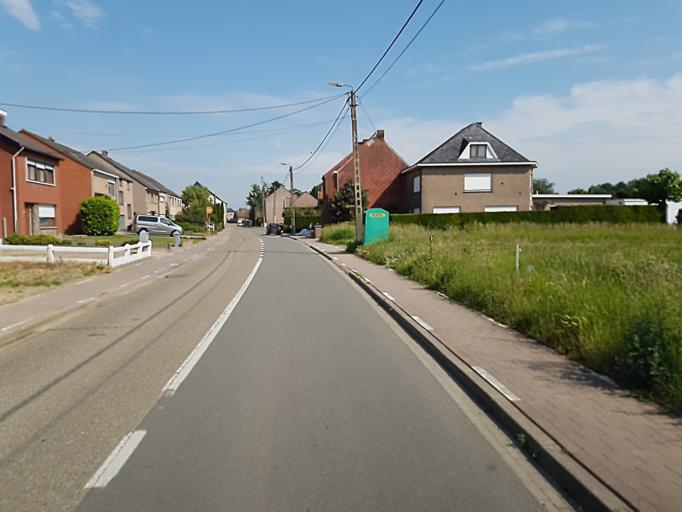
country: BE
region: Flanders
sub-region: Provincie Vlaams-Brabant
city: Herent
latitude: 50.9150
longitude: 4.6990
